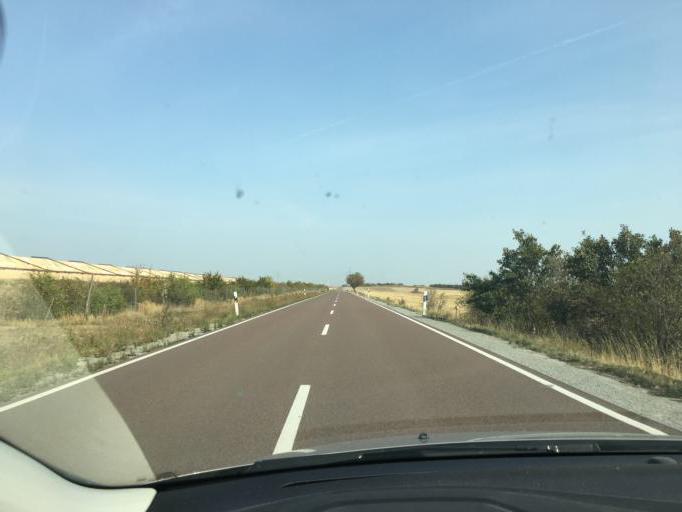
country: DE
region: Saxony-Anhalt
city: Baalberge
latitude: 51.8080
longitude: 11.8173
